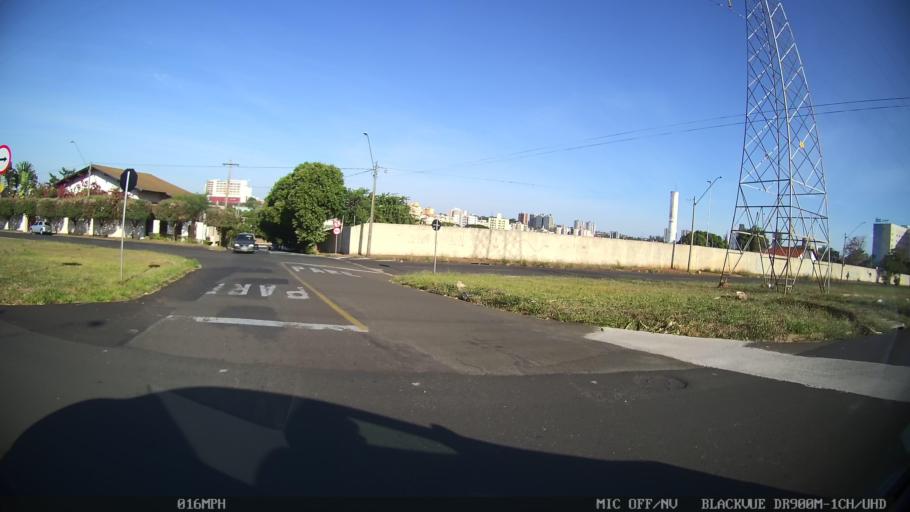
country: BR
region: Sao Paulo
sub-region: Sao Jose Do Rio Preto
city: Sao Jose do Rio Preto
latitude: -20.8229
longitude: -49.4046
